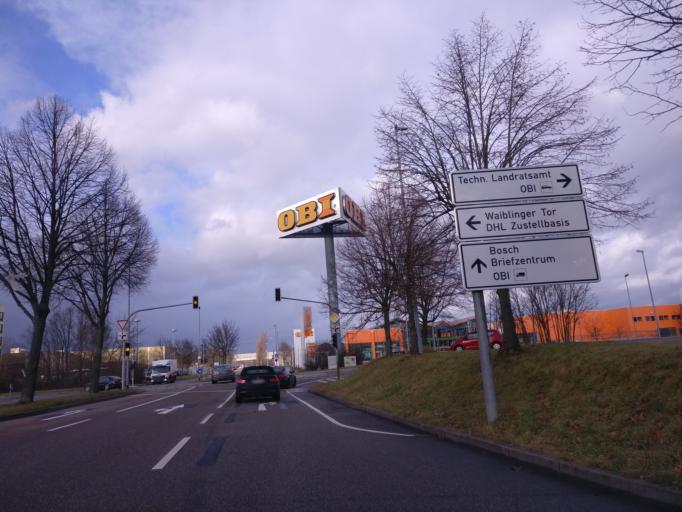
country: DE
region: Baden-Wuerttemberg
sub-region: Regierungsbezirk Stuttgart
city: Waiblingen
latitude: 48.8217
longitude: 9.2979
